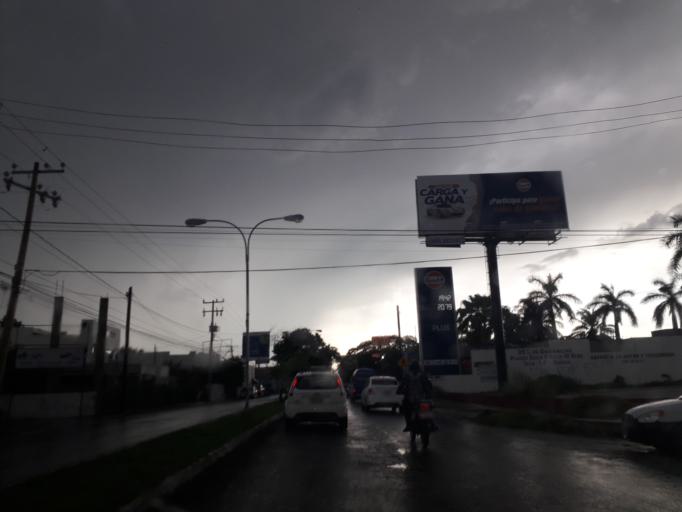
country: MX
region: Yucatan
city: Merida
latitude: 20.9793
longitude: -89.6470
